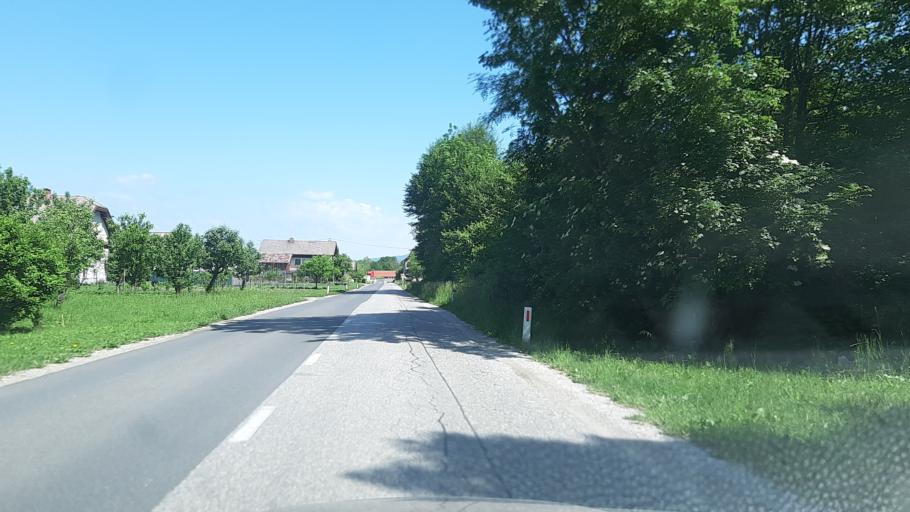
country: SI
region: Borovnica
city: Borovnica
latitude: 45.9315
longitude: 14.3633
